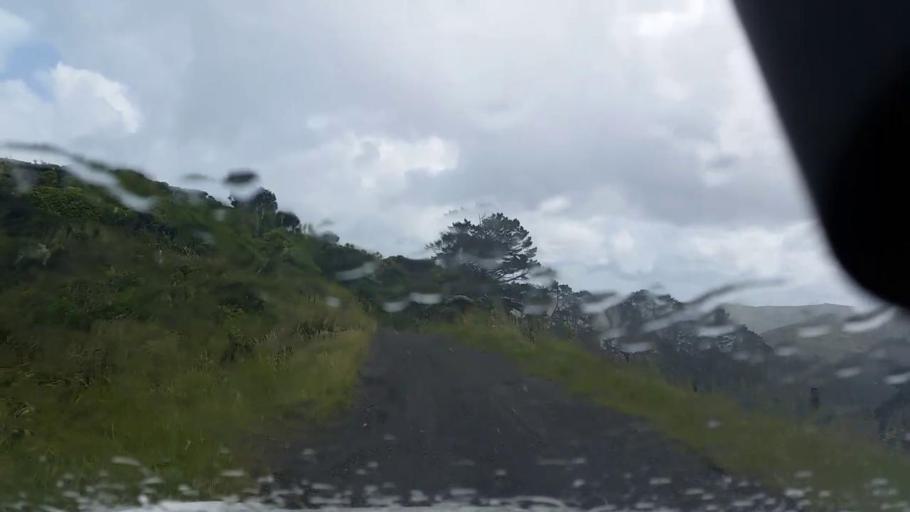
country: NZ
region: Auckland
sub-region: Auckland
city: Muriwai Beach
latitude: -36.9267
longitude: 174.4592
